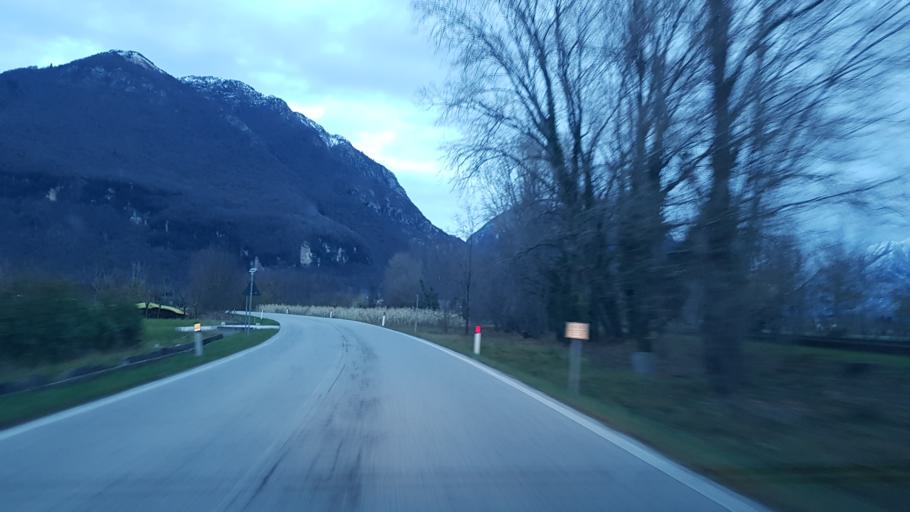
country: IT
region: Friuli Venezia Giulia
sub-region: Provincia di Udine
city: Gemona
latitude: 46.2773
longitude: 13.1005
